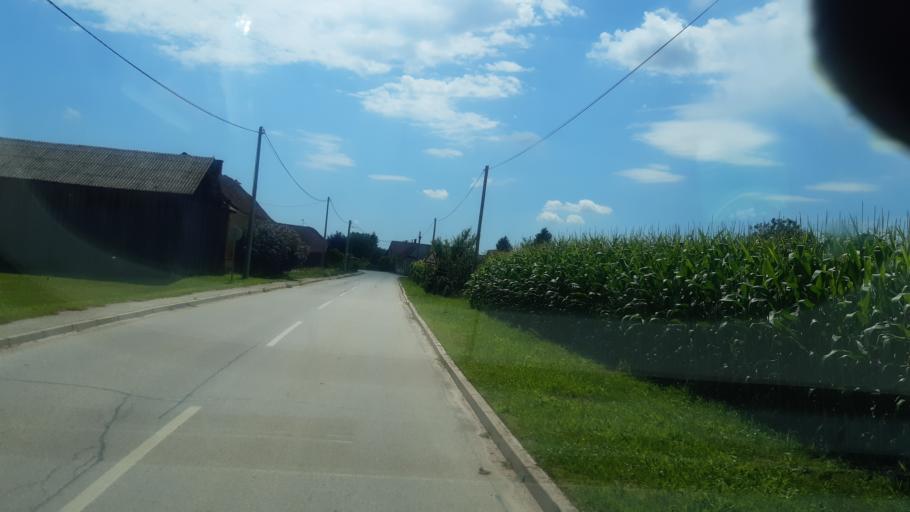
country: SI
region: Moravske Toplice
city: Moravske Toplice
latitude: 46.6711
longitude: 16.2062
